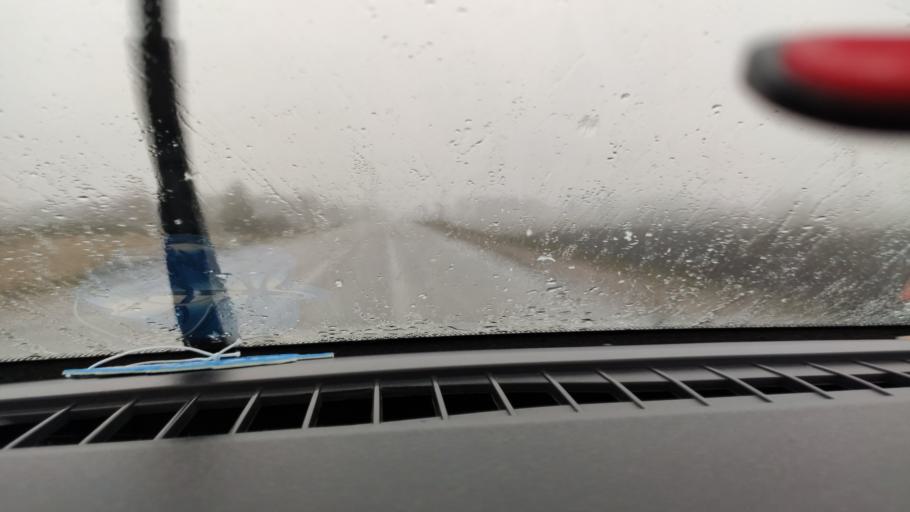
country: RU
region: Tatarstan
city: Cheremshan
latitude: 54.7235
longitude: 51.2974
